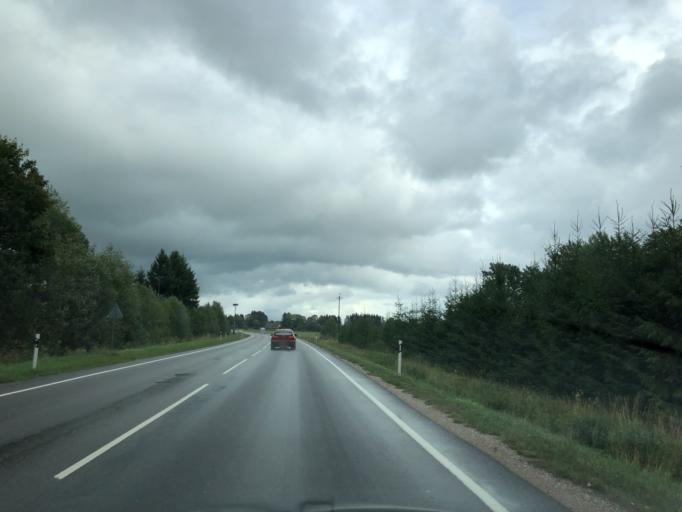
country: EE
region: Laeaene
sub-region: Ridala Parish
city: Uuemoisa
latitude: 58.9590
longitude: 23.8135
